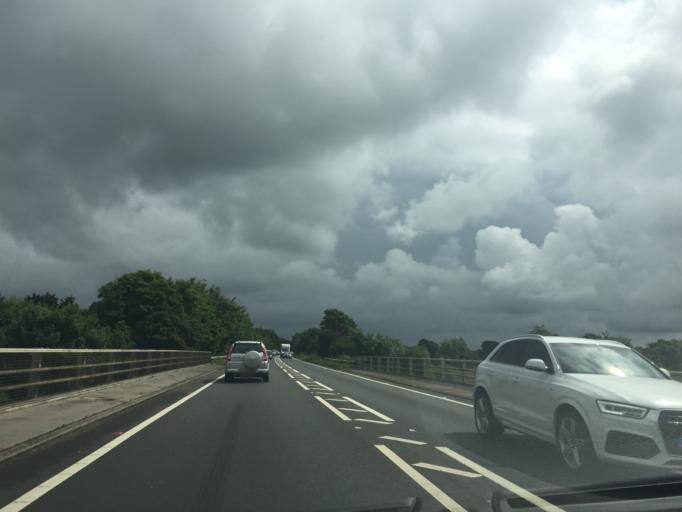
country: GB
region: England
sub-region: Dorset
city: Wimborne Minster
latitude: 50.7913
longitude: -1.9674
